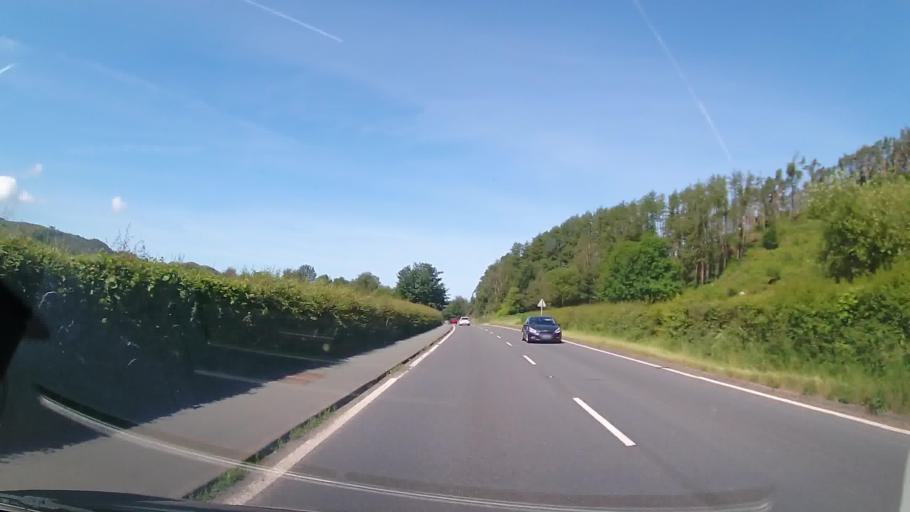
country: GB
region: Wales
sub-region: Sir Powys
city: Machynlleth
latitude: 52.5921
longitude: -3.8257
